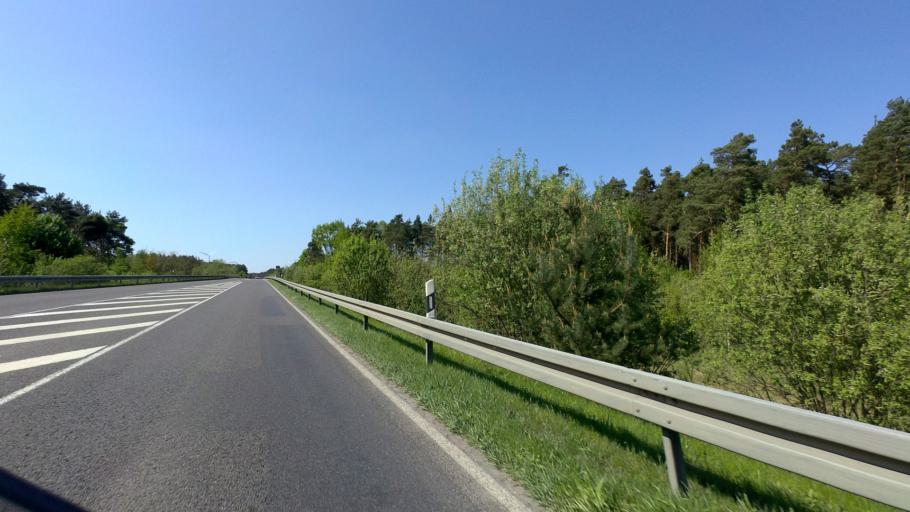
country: DE
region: Brandenburg
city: Beeskow
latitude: 52.1942
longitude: 14.2726
